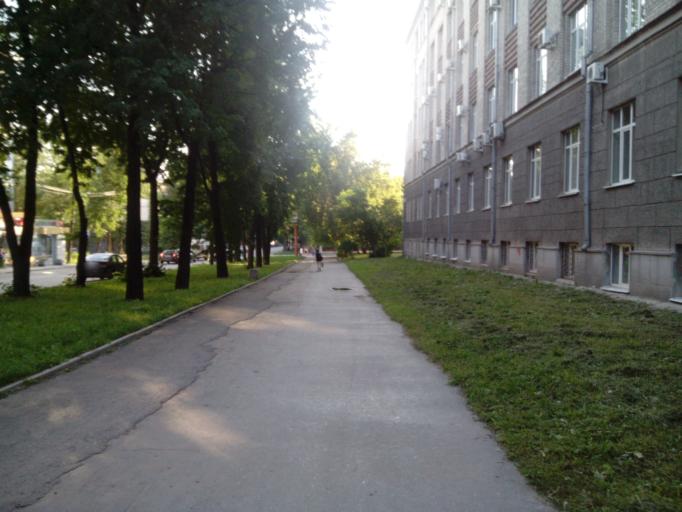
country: RU
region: Sverdlovsk
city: Yekaterinburg
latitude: 56.8476
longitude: 60.6558
